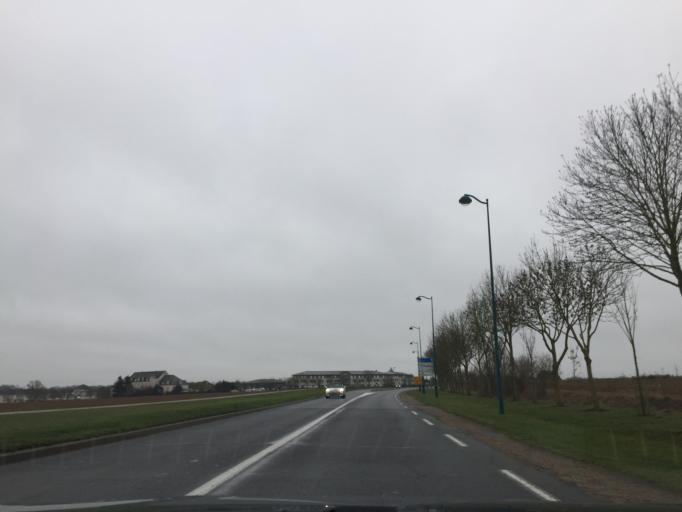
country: FR
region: Ile-de-France
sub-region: Departement de Seine-et-Marne
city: Magny-le-Hongre
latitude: 48.8701
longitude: 2.8064
